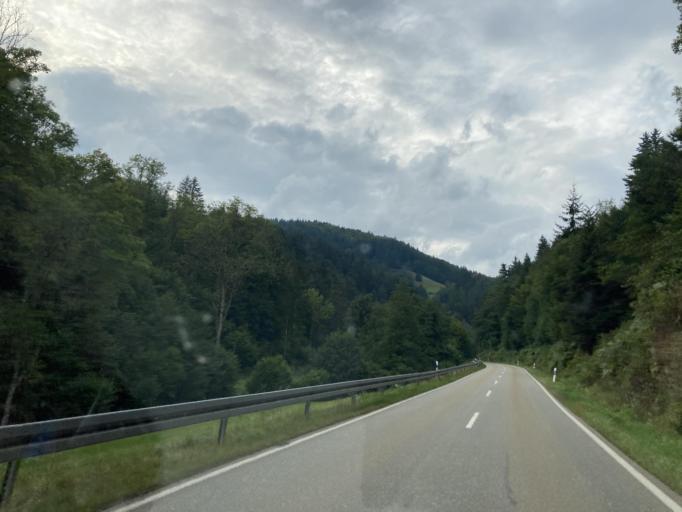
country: DE
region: Baden-Wuerttemberg
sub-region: Freiburg Region
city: Schonenberg
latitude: 47.7833
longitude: 7.8601
